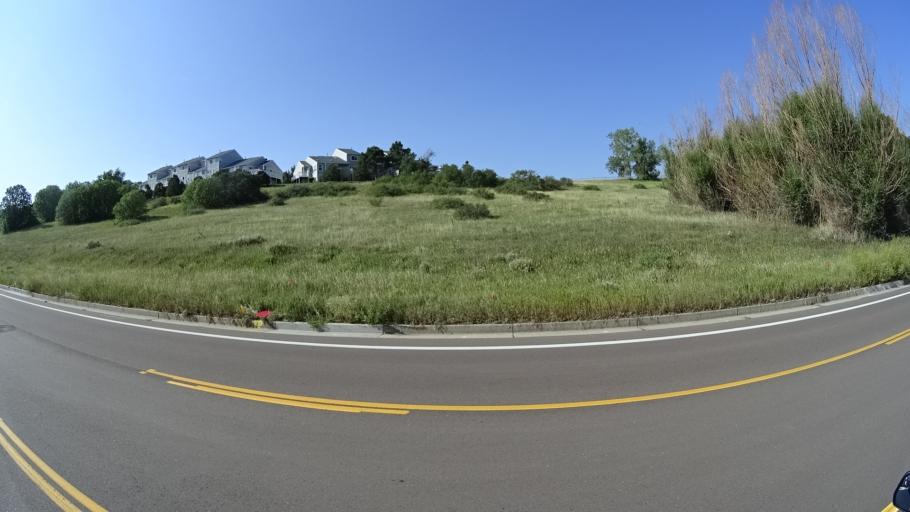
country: US
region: Colorado
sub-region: El Paso County
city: Air Force Academy
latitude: 38.9490
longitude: -104.7816
